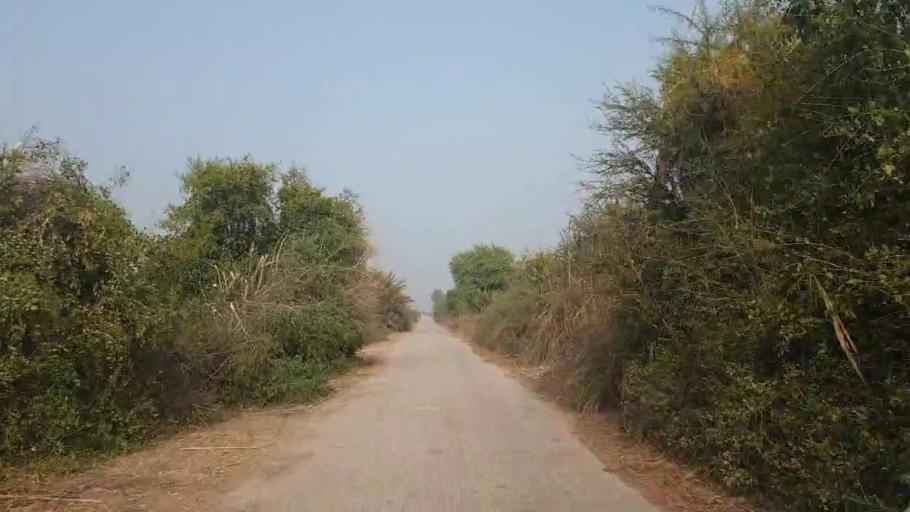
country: PK
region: Sindh
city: Shahdadpur
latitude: 25.8869
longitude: 68.5874
